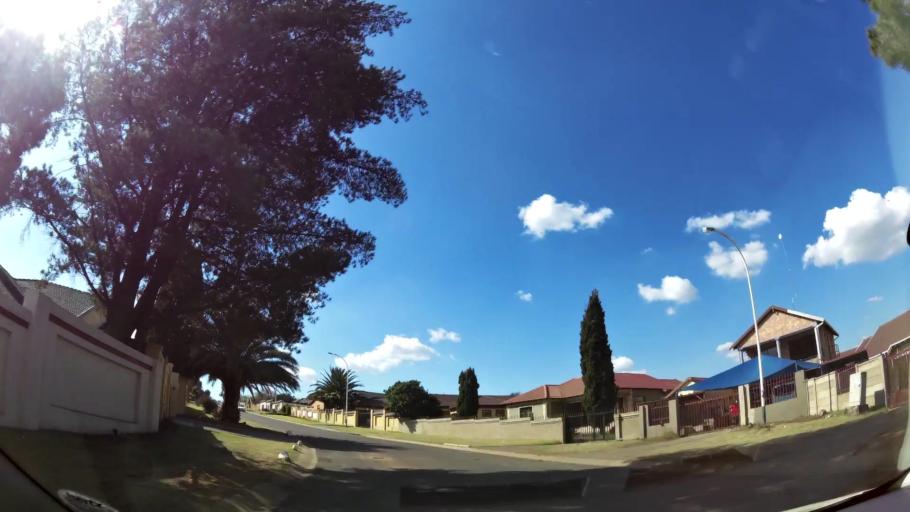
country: ZA
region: Mpumalanga
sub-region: Nkangala District Municipality
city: Witbank
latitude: -25.9311
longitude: 29.2468
